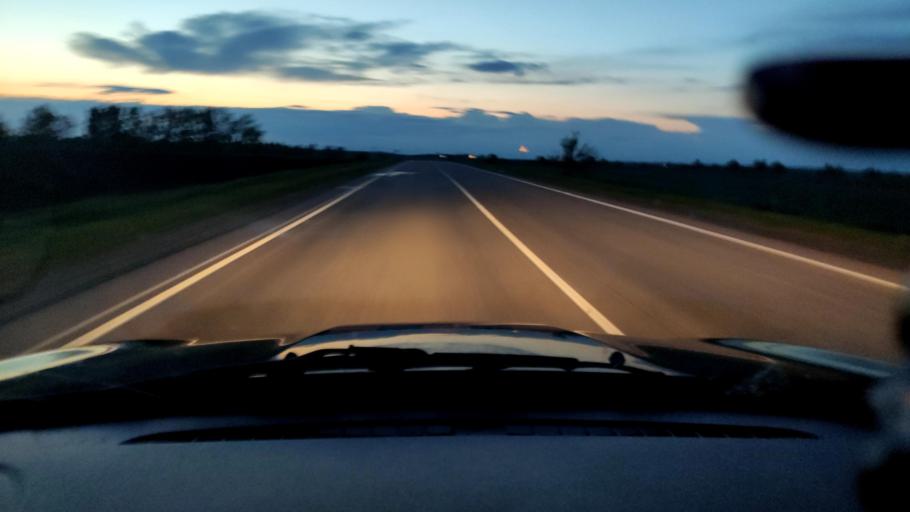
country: RU
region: Voronezj
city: Shilovo
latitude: 51.4611
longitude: 38.9696
